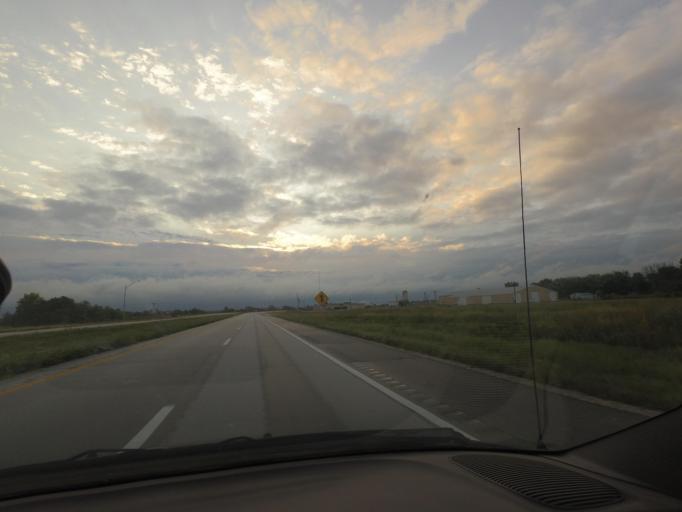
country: US
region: Missouri
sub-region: Shelby County
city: Shelbina
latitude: 39.6978
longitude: -92.0368
